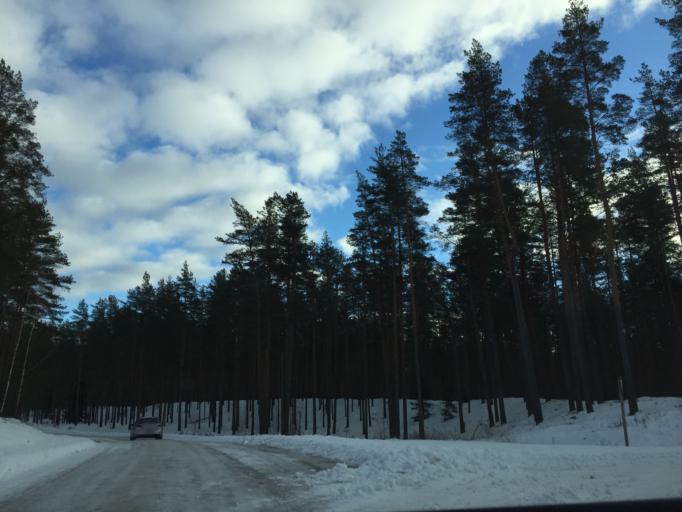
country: LV
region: Lielvarde
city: Lielvarde
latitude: 56.5606
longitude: 24.8446
